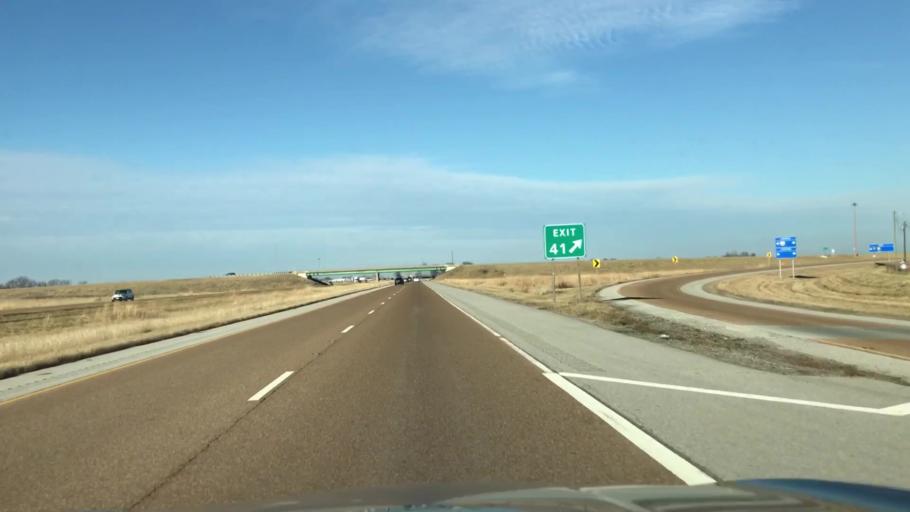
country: US
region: Illinois
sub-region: Macoupin County
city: Staunton
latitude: 39.0172
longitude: -89.7494
